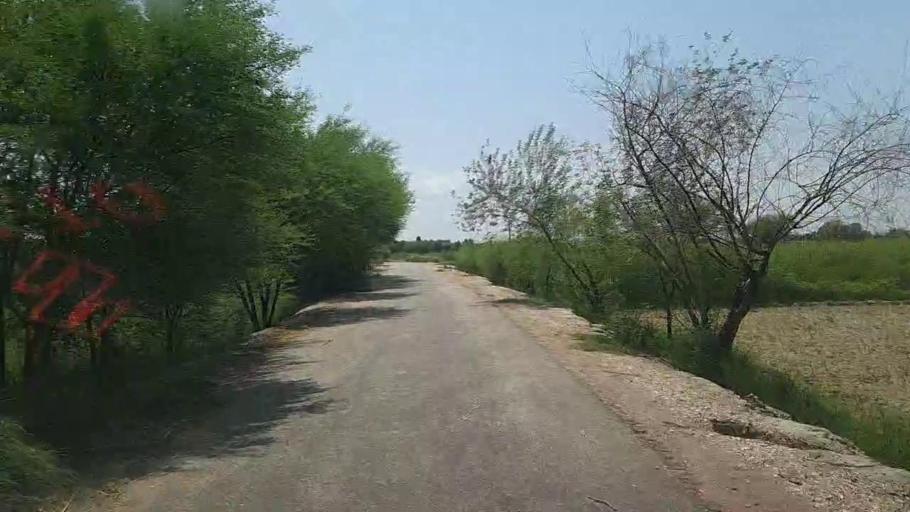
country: PK
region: Sindh
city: Ubauro
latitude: 28.1505
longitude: 69.7733
